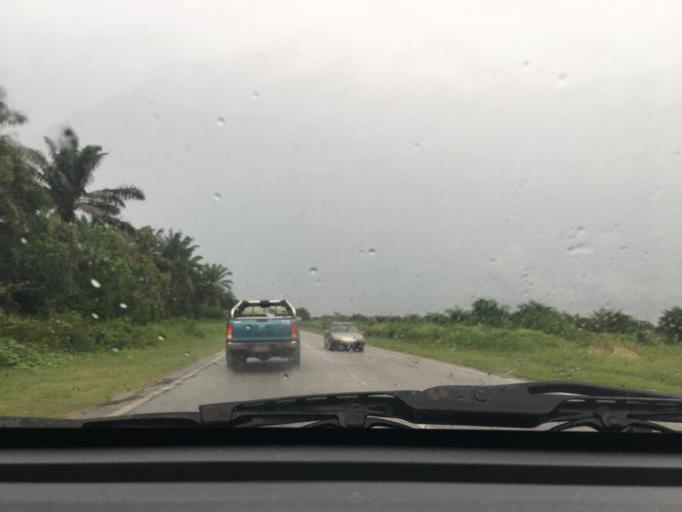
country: MY
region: Kedah
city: Sungai Petani
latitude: 5.6002
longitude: 100.6397
